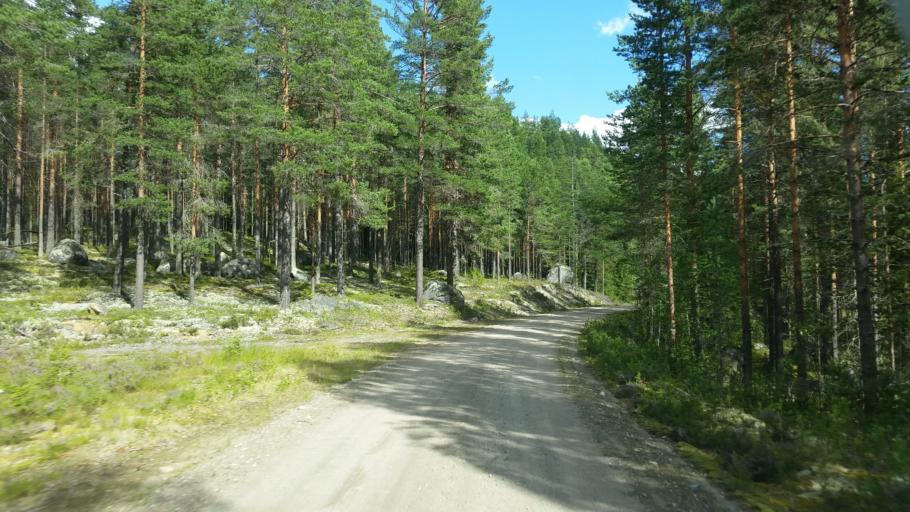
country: SE
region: Gaevleborg
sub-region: Ljusdals Kommun
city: Ljusdal
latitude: 61.9774
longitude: 16.2030
